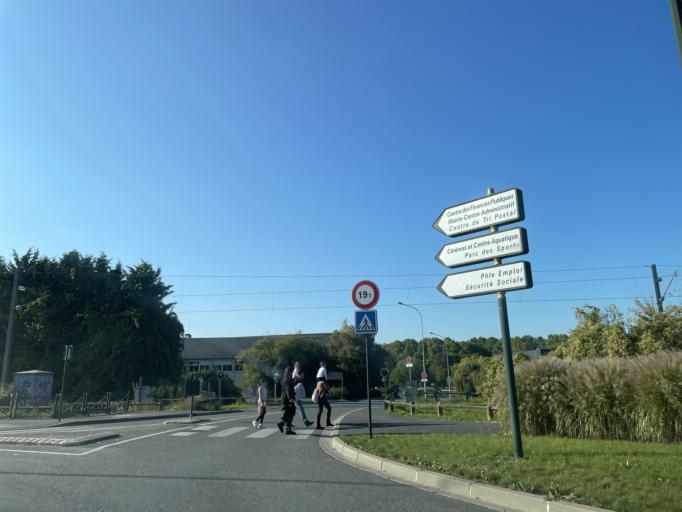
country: FR
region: Ile-de-France
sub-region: Departement de Seine-et-Marne
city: Coulommiers
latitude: 48.8082
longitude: 3.0921
